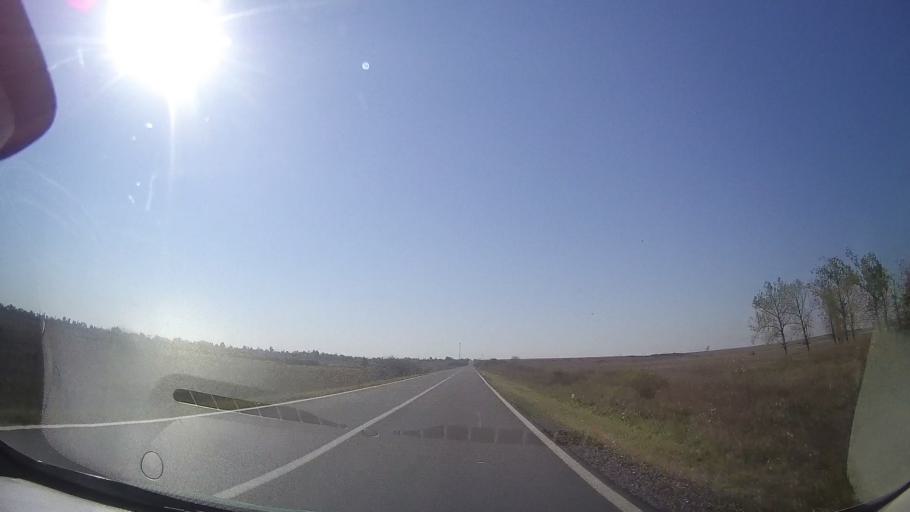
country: RO
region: Timis
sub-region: Comuna Belint
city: Belint
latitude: 45.7757
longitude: 21.7313
